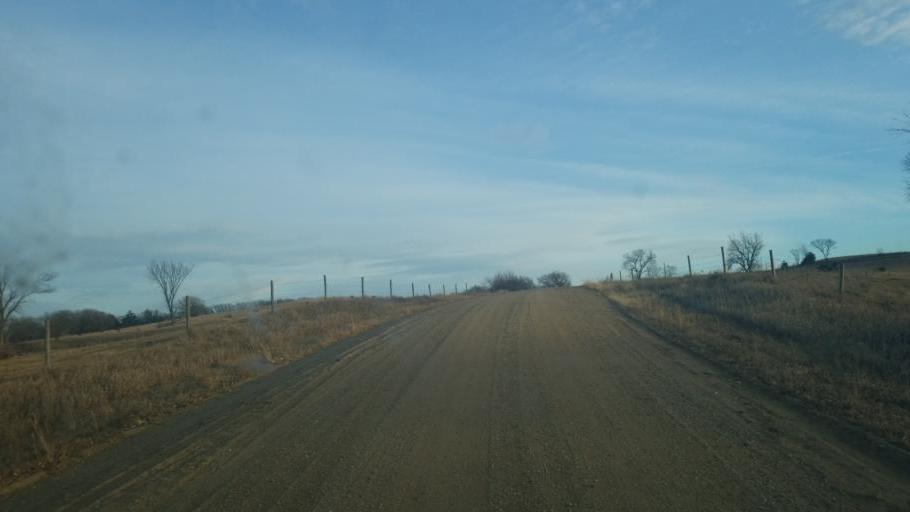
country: US
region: Nebraska
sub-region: Knox County
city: Center
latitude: 42.6946
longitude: -97.7852
